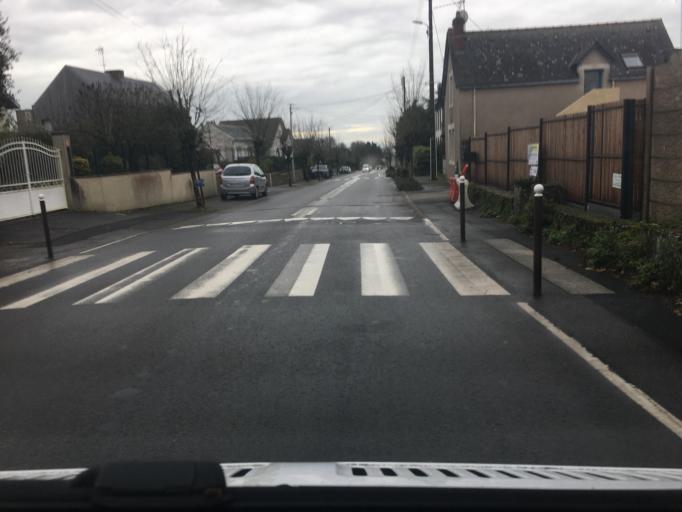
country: FR
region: Pays de la Loire
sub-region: Departement de la Loire-Atlantique
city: Guerande
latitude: 47.3222
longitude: -2.4286
